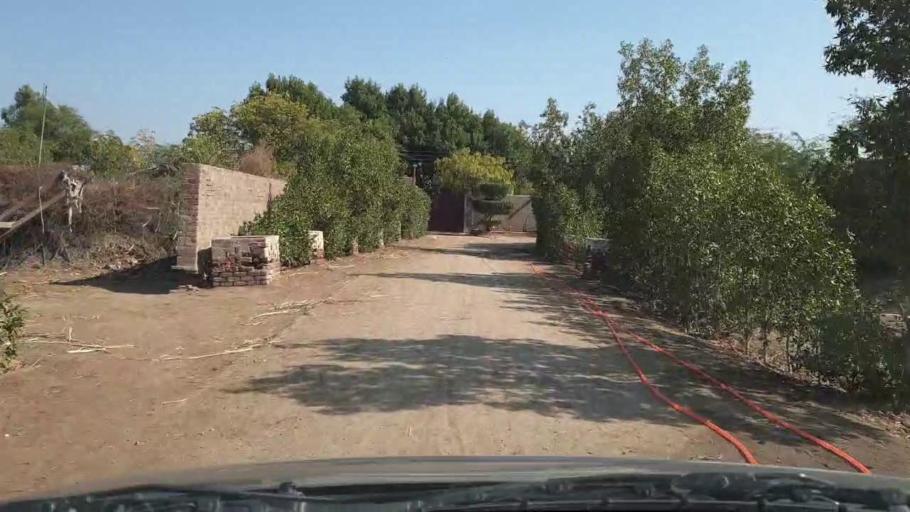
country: PK
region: Sindh
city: Samaro
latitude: 25.2234
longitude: 69.2660
